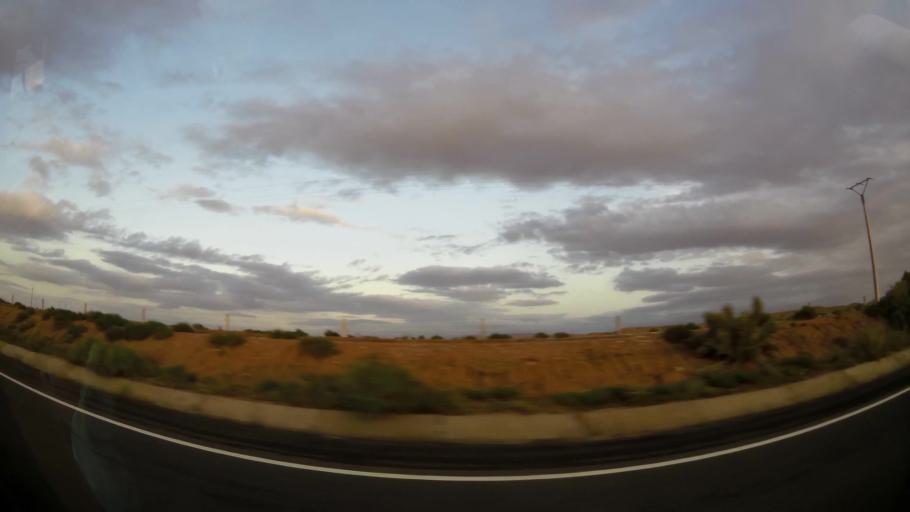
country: MA
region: Oriental
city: Taourirt
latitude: 34.5406
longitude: -2.9113
